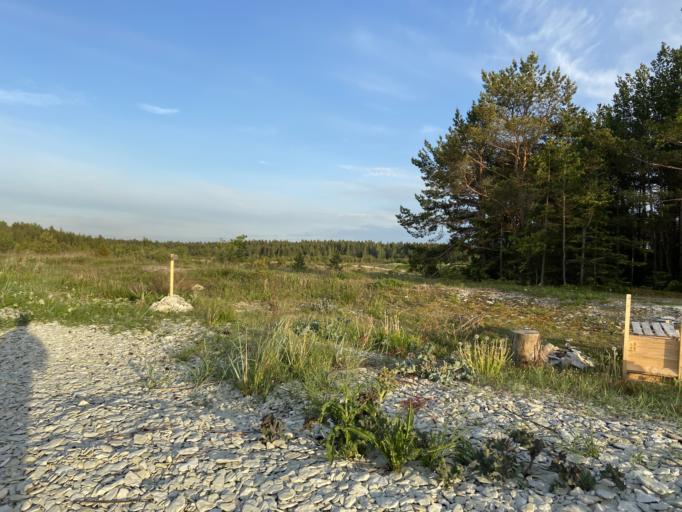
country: EE
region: Harju
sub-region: Paldiski linn
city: Paldiski
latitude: 59.2705
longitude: 23.7375
